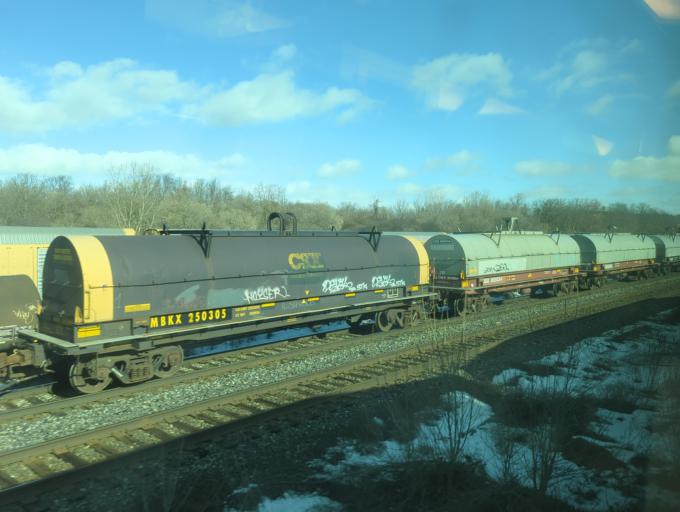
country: CA
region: Ontario
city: Hamilton
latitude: 43.3142
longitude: -79.8530
